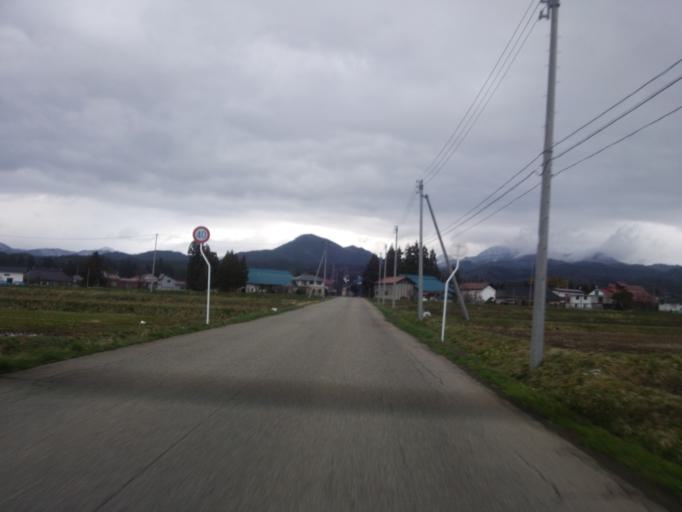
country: JP
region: Fukushima
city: Kitakata
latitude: 37.6637
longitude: 139.9063
